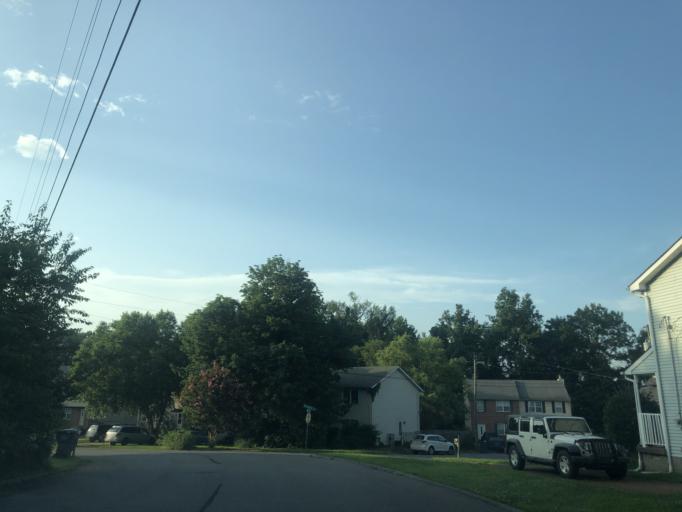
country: US
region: Tennessee
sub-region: Davidson County
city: Lakewood
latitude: 36.1468
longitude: -86.6404
